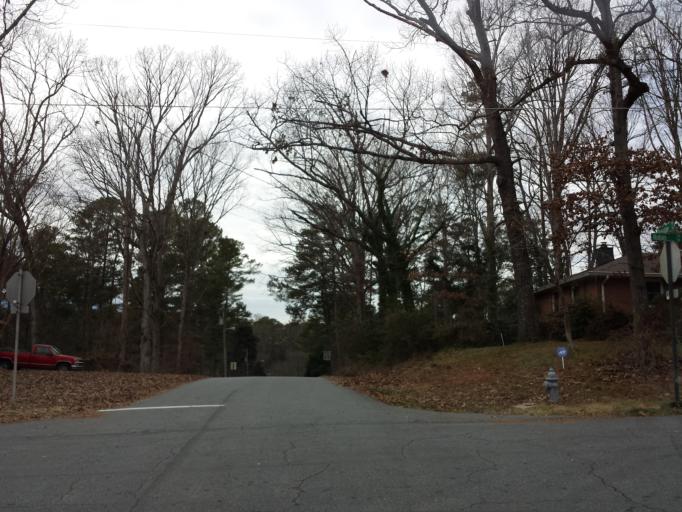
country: US
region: Georgia
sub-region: Cobb County
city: Fair Oaks
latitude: 33.9416
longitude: -84.4866
